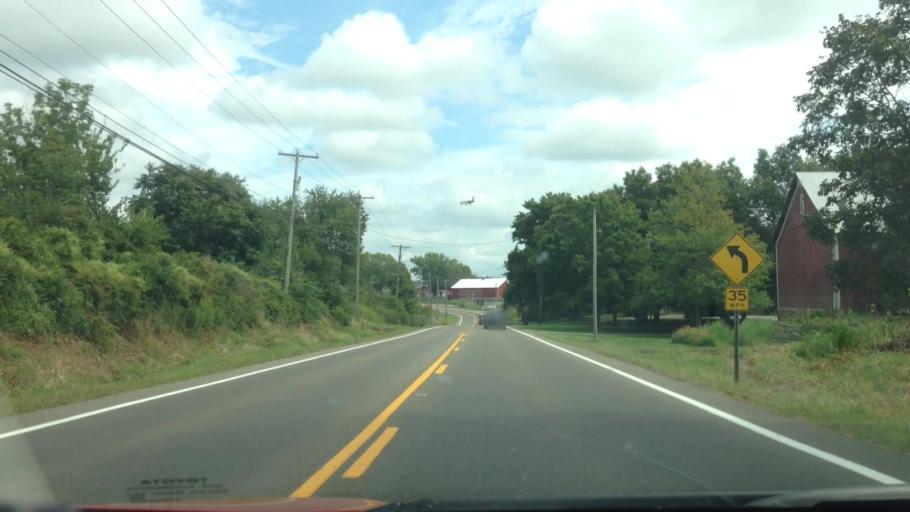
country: US
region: Ohio
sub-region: Summit County
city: Greensburg
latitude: 40.8976
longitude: -81.4728
